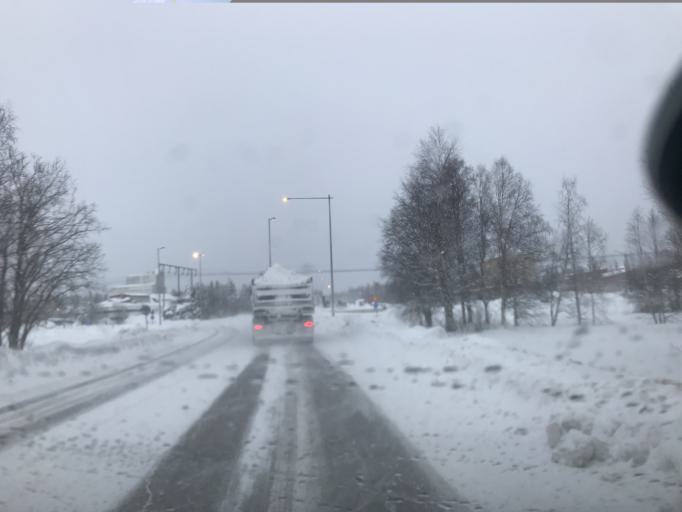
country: SE
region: Norrbotten
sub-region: Lulea Kommun
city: Lulea
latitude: 65.6144
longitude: 22.1331
